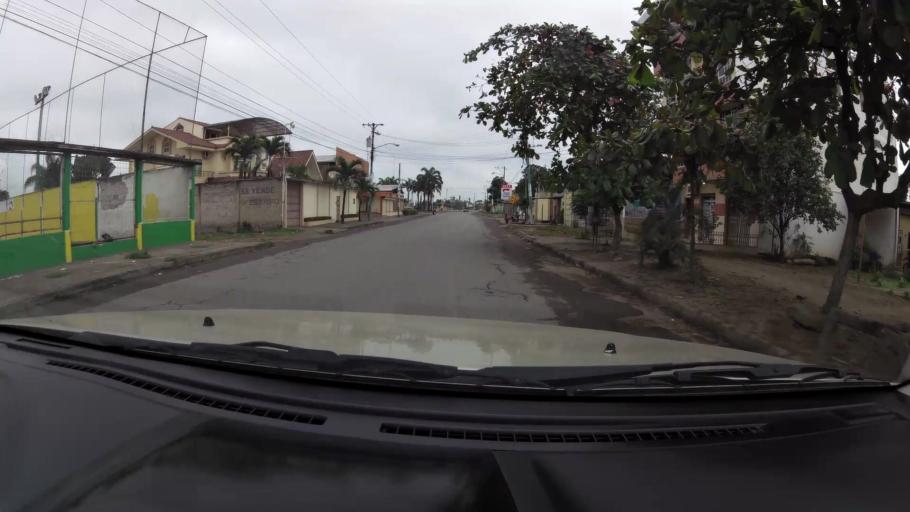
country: EC
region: El Oro
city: Pasaje
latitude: -3.3270
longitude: -79.8236
